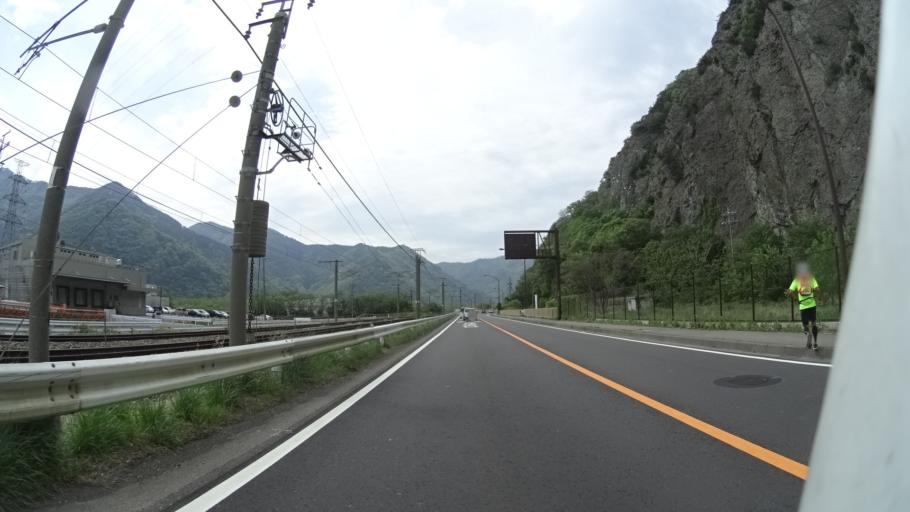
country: JP
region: Nagano
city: Ueda
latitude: 36.4211
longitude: 138.1981
